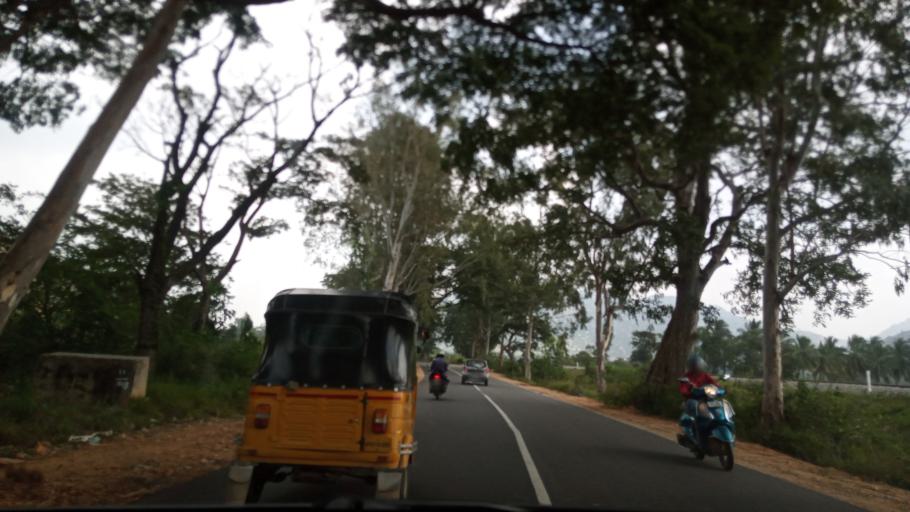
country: IN
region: Andhra Pradesh
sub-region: Chittoor
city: Madanapalle
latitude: 13.6374
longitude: 78.5776
